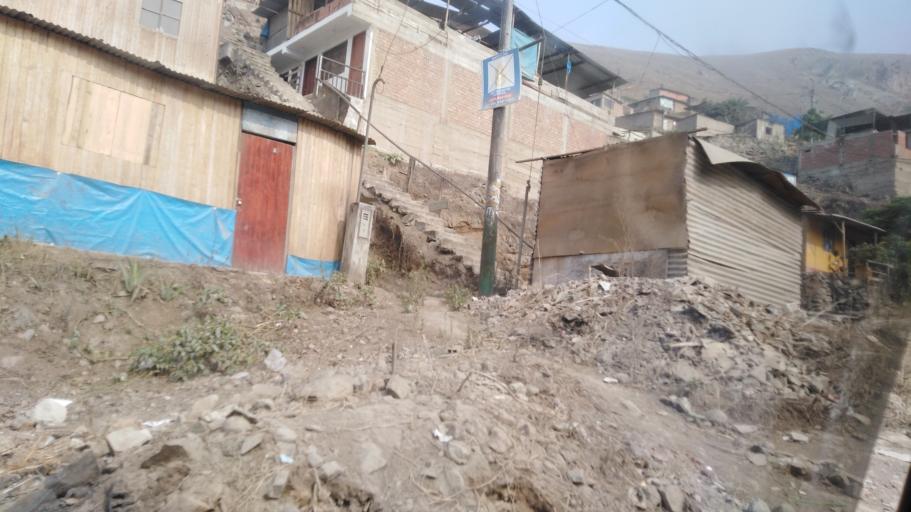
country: PE
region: Lima
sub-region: Lima
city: La Molina
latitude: -12.1430
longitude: -76.9250
